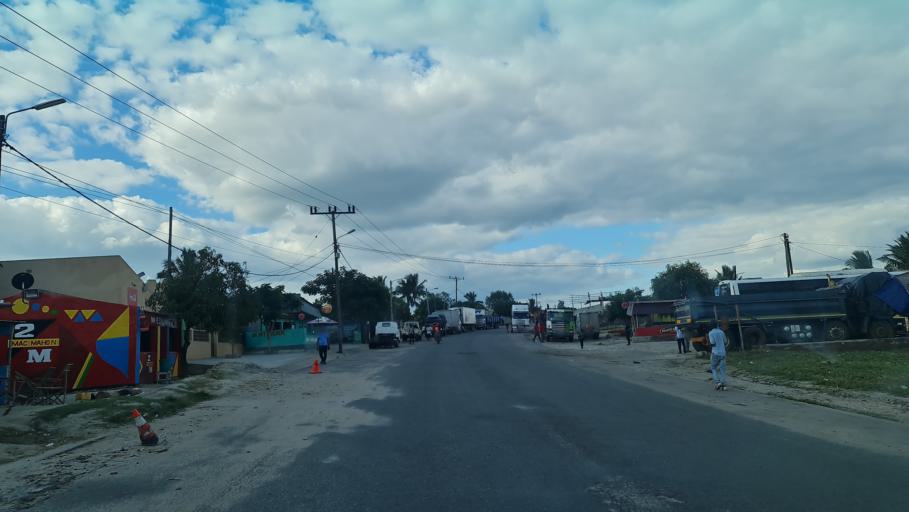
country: MZ
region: Manica
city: Chimoio
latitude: -19.2110
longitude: 33.9254
